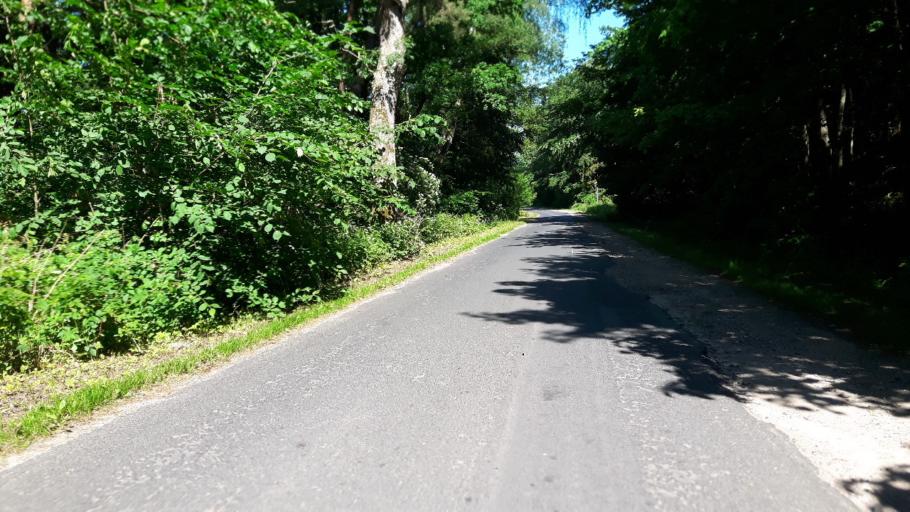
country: PL
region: Pomeranian Voivodeship
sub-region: Powiat slupski
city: Glowczyce
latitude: 54.6398
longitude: 17.4117
